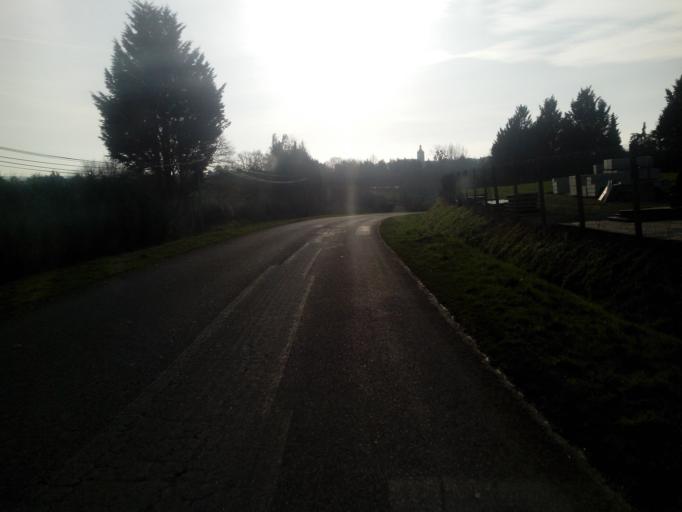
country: FR
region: Brittany
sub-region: Departement du Morbihan
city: Mauron
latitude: 48.0896
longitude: -2.2783
